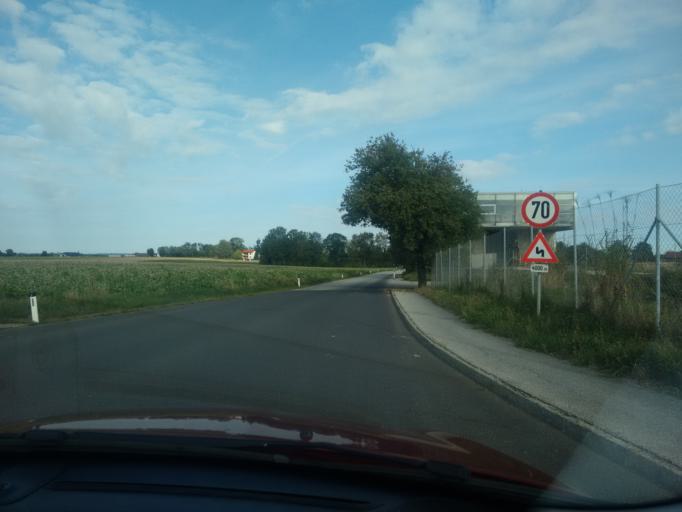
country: AT
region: Upper Austria
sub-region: Wels-Land
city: Steinhaus
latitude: 48.1191
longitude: 14.0283
